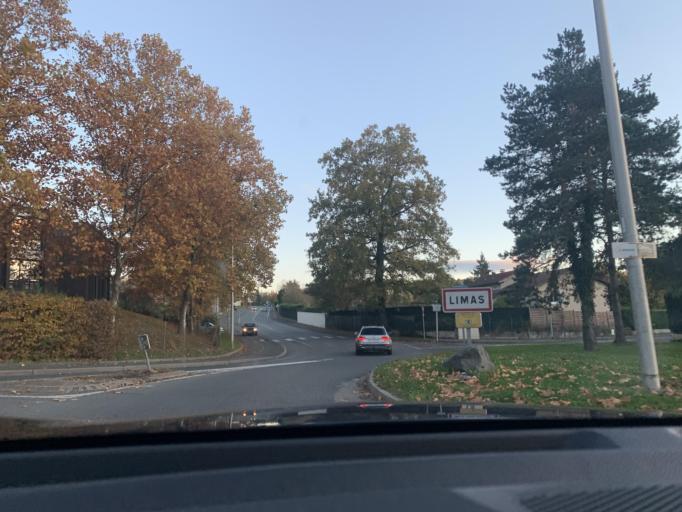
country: FR
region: Rhone-Alpes
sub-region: Departement du Rhone
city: Limas
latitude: 45.9802
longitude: 4.6980
